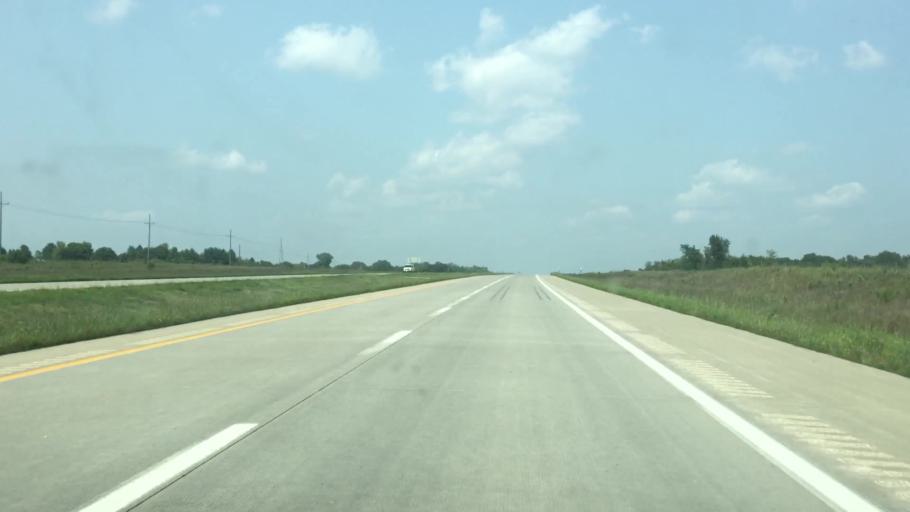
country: US
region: Kansas
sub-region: Douglas County
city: Baldwin City
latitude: 38.7279
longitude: -95.2683
